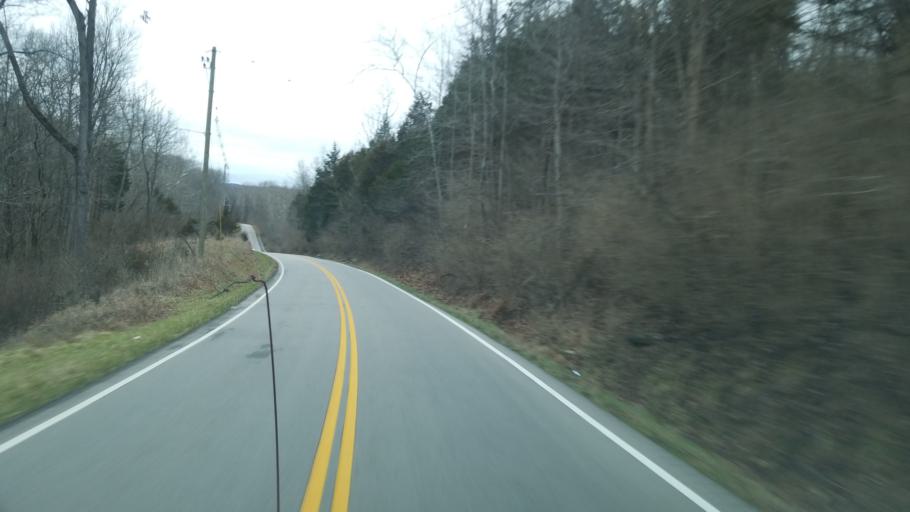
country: US
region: Ohio
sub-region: Clermont County
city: New Richmond
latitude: 38.8742
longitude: -84.2424
